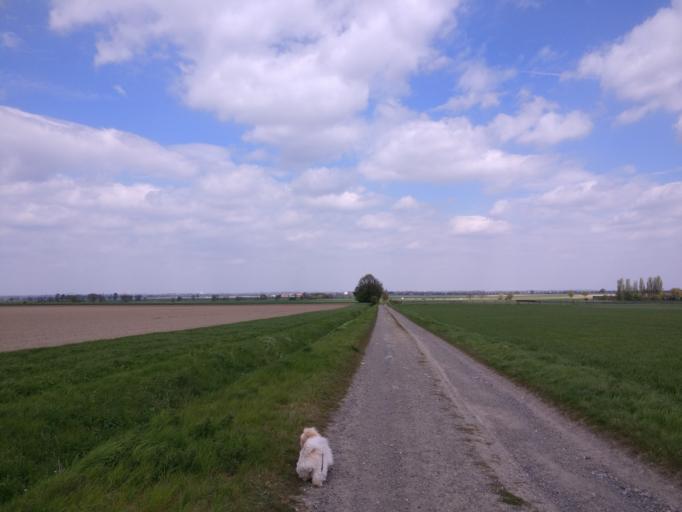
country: DE
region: Lower Saxony
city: Schellerten
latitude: 52.1362
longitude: 10.0570
